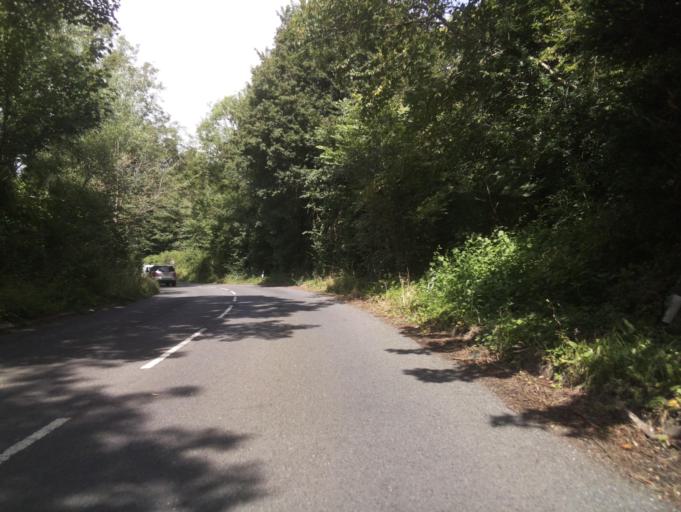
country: GB
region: England
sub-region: Dorset
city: Blandford Forum
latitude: 50.8697
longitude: -2.1710
